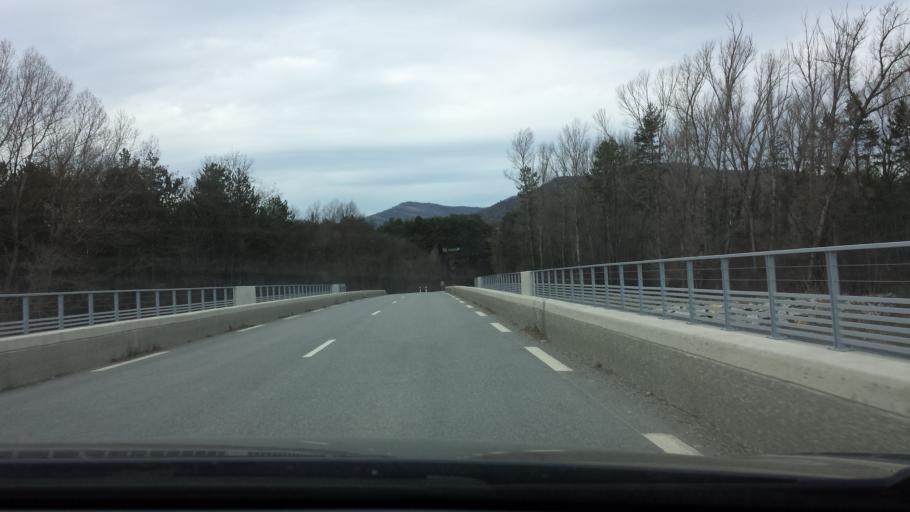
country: FR
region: Provence-Alpes-Cote d'Azur
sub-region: Departement des Alpes-de-Haute-Provence
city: Mallemoisson
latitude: 44.0403
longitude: 6.1426
